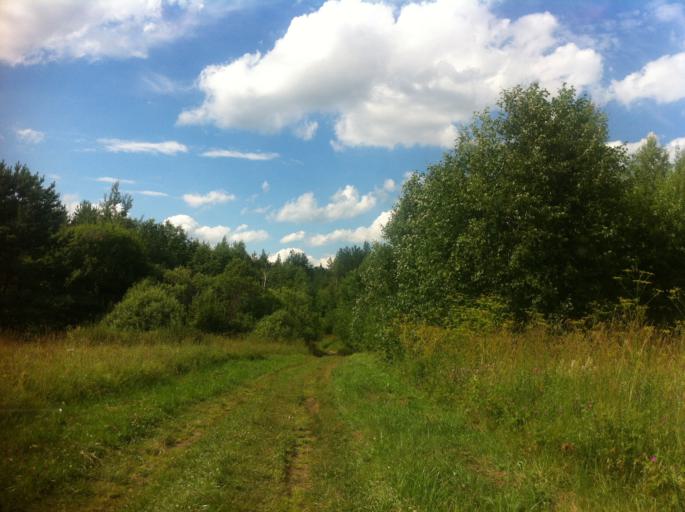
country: RU
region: Pskov
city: Izborsk
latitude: 57.8164
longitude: 27.9492
